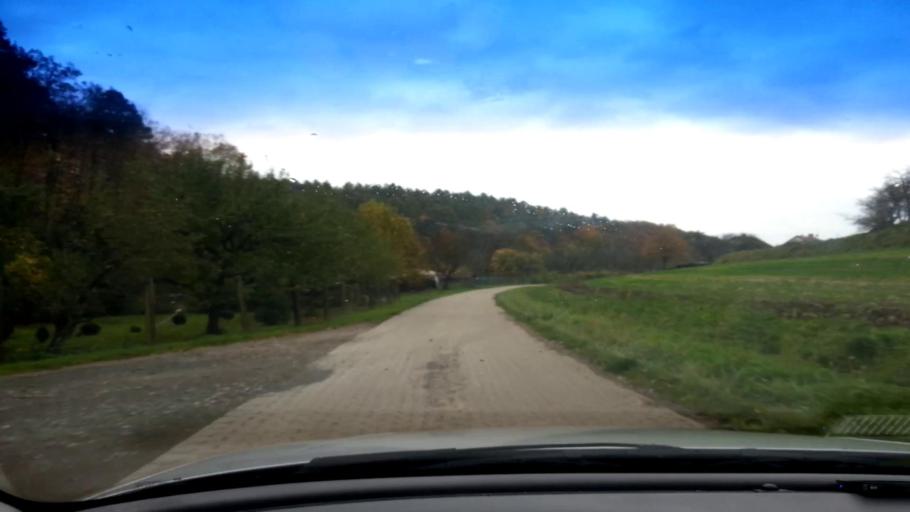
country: DE
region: Bavaria
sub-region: Regierungsbezirk Unterfranken
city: Stettfeld
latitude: 49.9773
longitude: 10.7309
